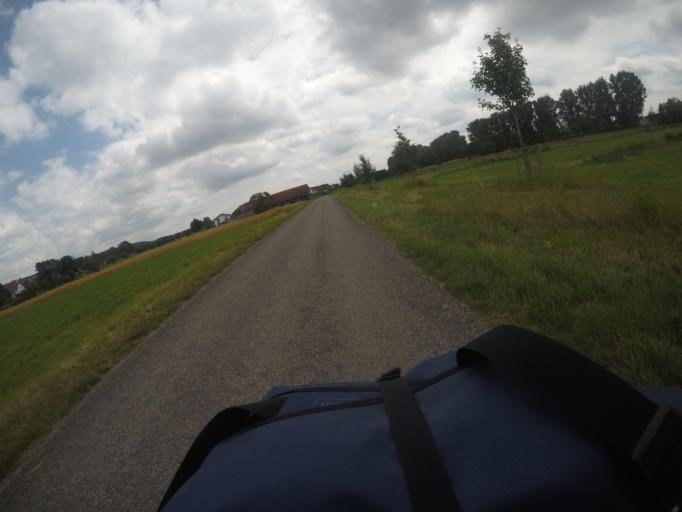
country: DE
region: Bavaria
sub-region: Swabia
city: Heimertingen
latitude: 48.0203
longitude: 10.1721
